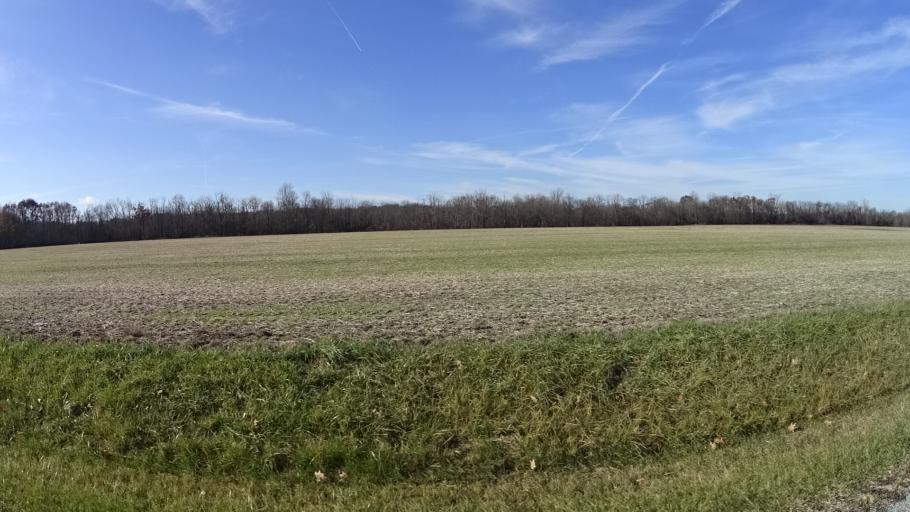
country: US
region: Ohio
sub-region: Lorain County
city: Wellington
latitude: 41.0951
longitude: -82.2008
